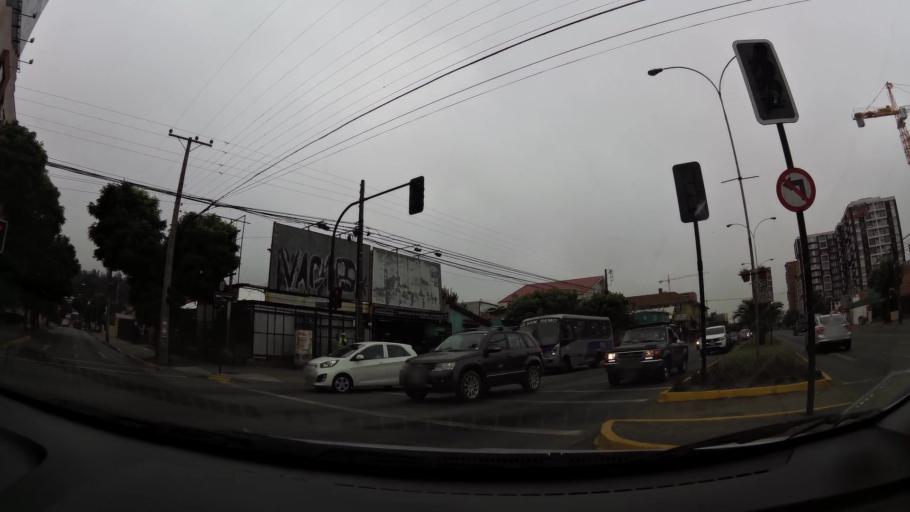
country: CL
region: Biobio
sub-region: Provincia de Concepcion
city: Concepcion
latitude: -36.8164
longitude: -73.0355
